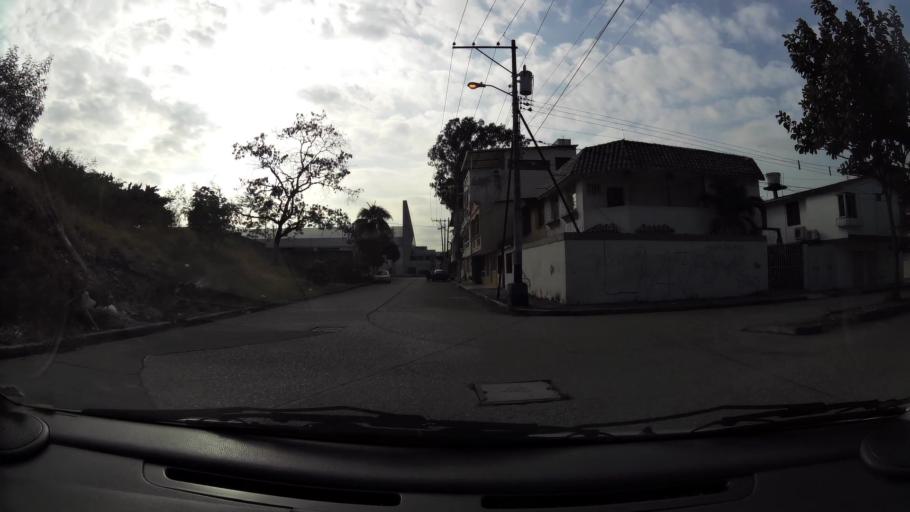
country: EC
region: Guayas
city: Eloy Alfaro
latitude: -2.1340
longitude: -79.8888
